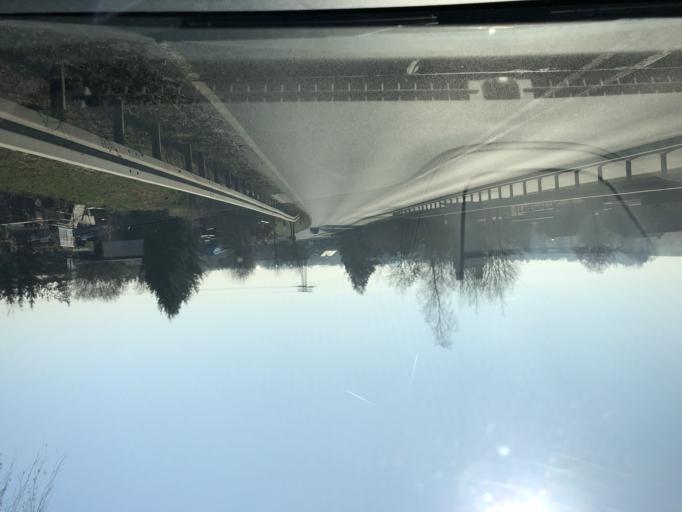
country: DE
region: Saxony
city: Ohorn
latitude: 51.1631
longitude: 14.0527
